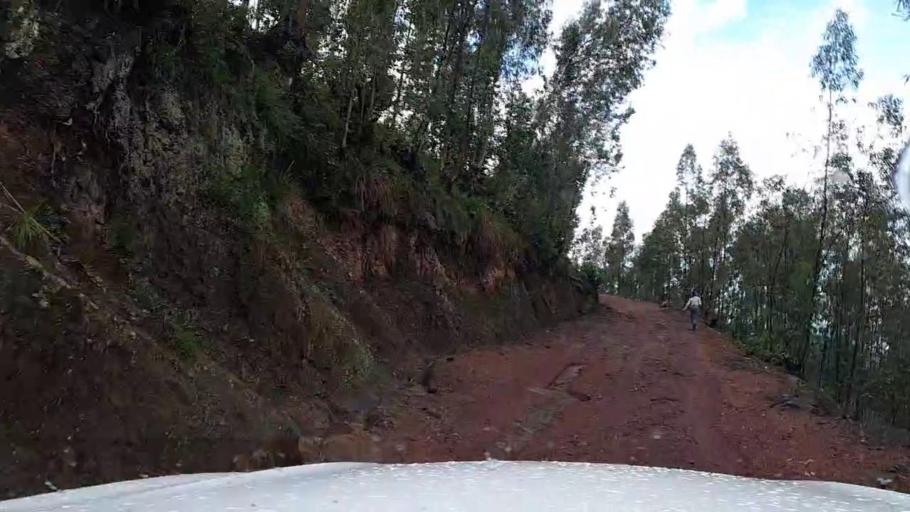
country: RW
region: Northern Province
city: Byumba
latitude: -1.7210
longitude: 29.9117
